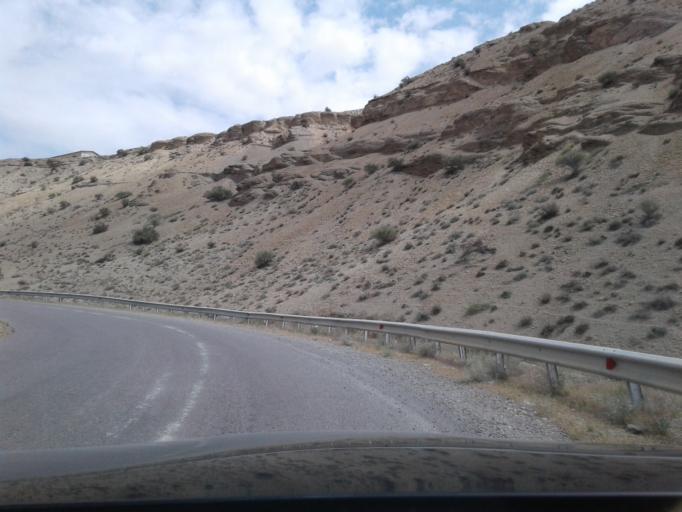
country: TM
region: Ahal
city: Baharly
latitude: 38.5036
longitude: 57.0811
